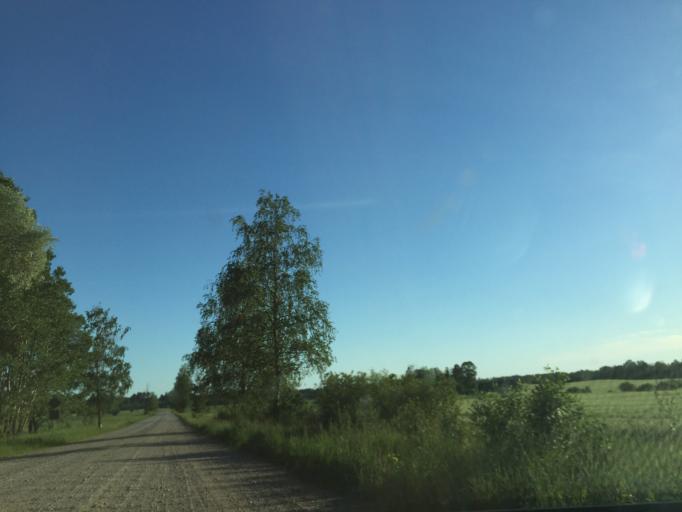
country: LV
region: Broceni
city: Broceni
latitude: 56.7848
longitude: 22.5623
